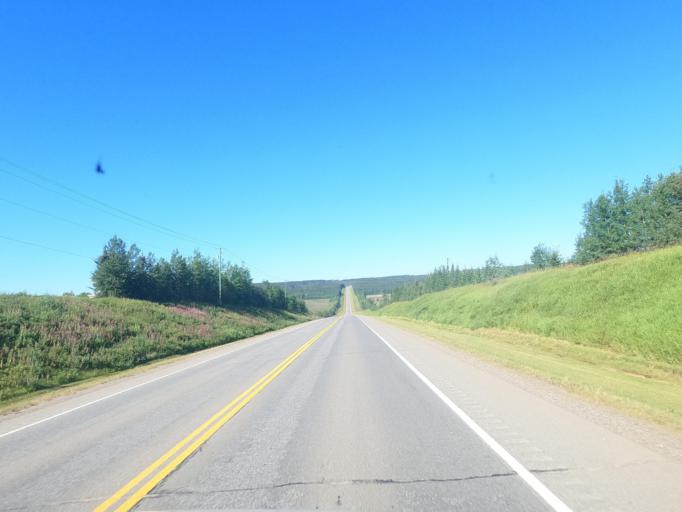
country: CA
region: British Columbia
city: Fort St. John
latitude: 56.6298
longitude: -121.5274
